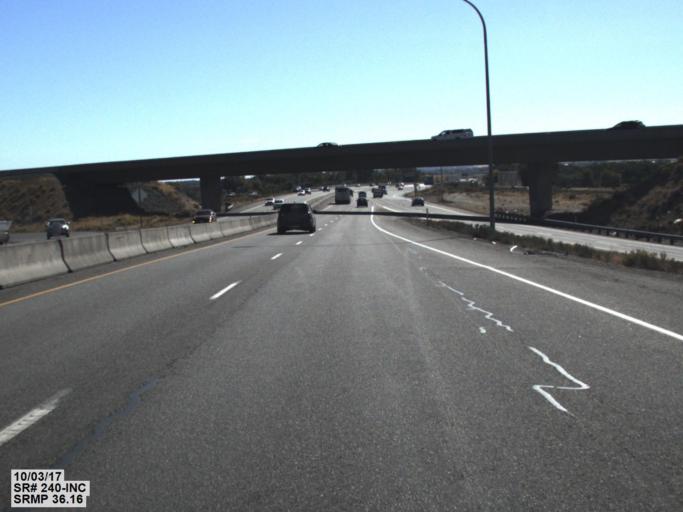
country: US
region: Washington
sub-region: Benton County
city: Richland
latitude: 46.2579
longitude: -119.2622
